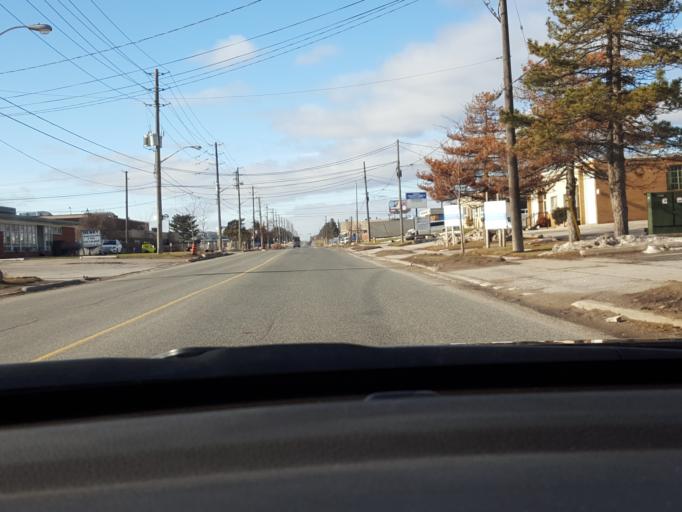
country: CA
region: Ontario
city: Concord
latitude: 43.7588
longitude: -79.5471
